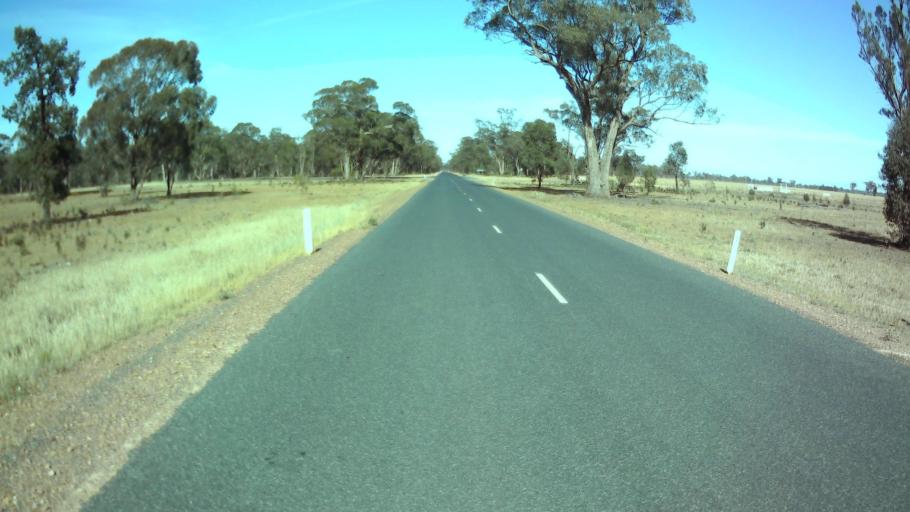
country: AU
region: New South Wales
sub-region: Weddin
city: Grenfell
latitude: -34.1127
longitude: 147.8451
